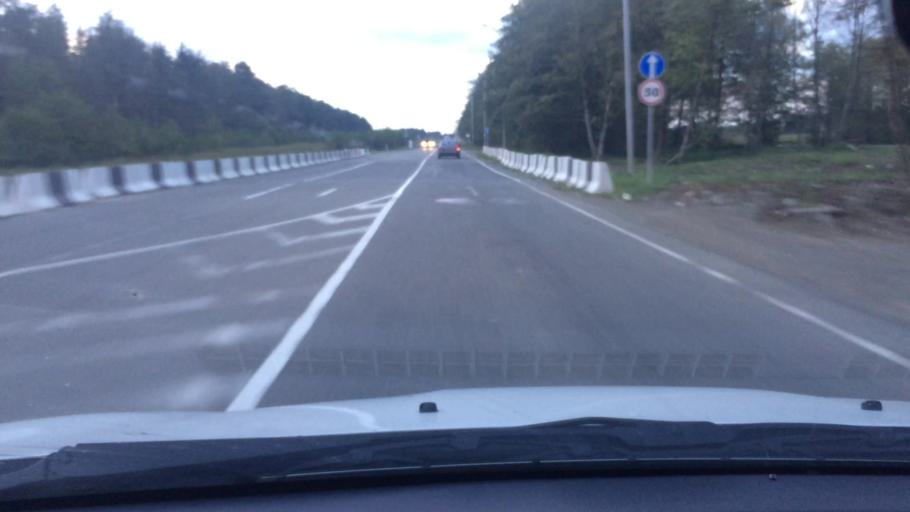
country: GE
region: Guria
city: Urek'i
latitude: 41.9433
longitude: 41.7708
